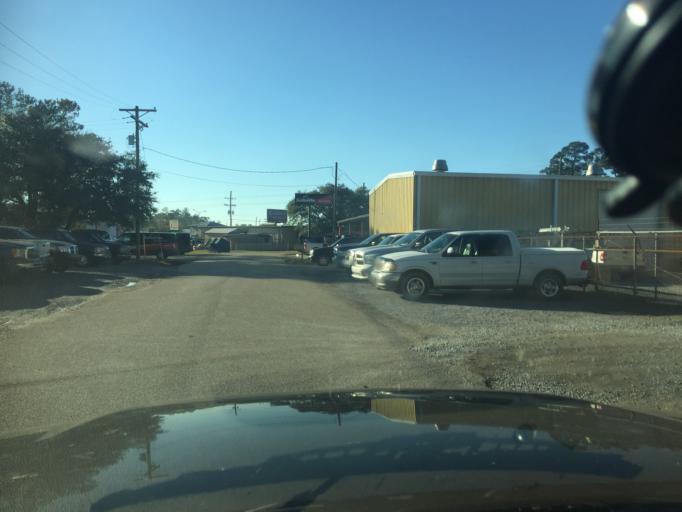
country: US
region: Louisiana
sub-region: Saint Tammany Parish
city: Slidell
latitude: 30.2530
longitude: -89.7673
